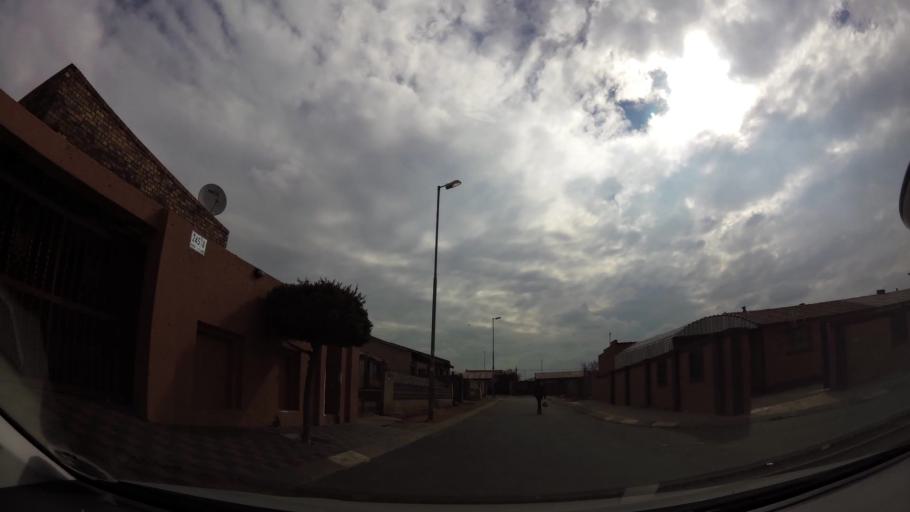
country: ZA
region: Gauteng
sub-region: City of Johannesburg Metropolitan Municipality
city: Soweto
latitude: -26.2701
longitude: 27.8592
